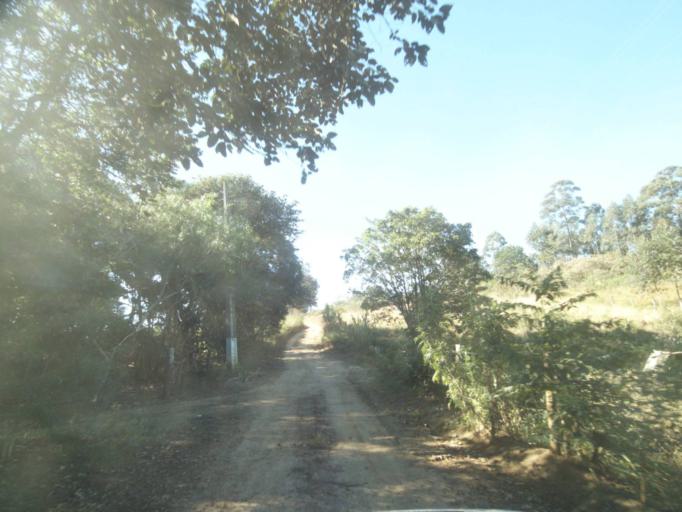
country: BR
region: Parana
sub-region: Tibagi
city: Tibagi
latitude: -24.5711
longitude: -50.4724
